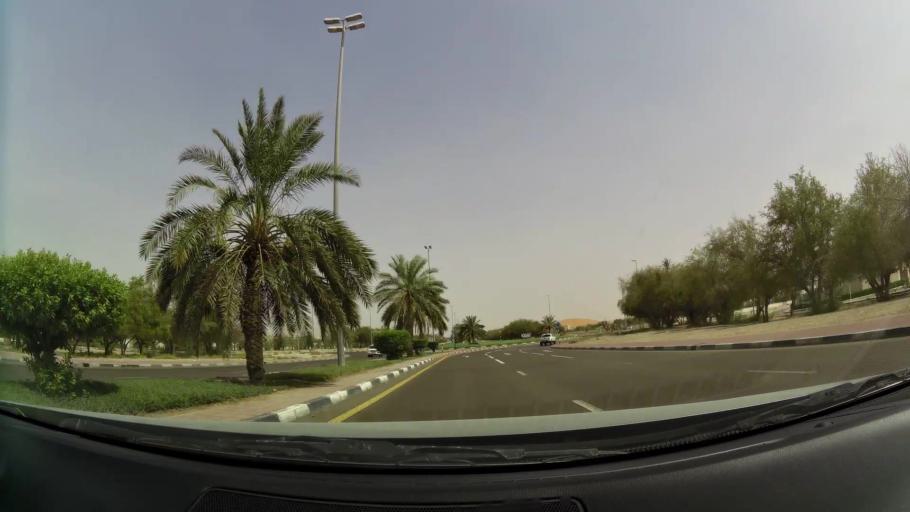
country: AE
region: Abu Dhabi
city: Al Ain
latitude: 24.1630
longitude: 55.6702
